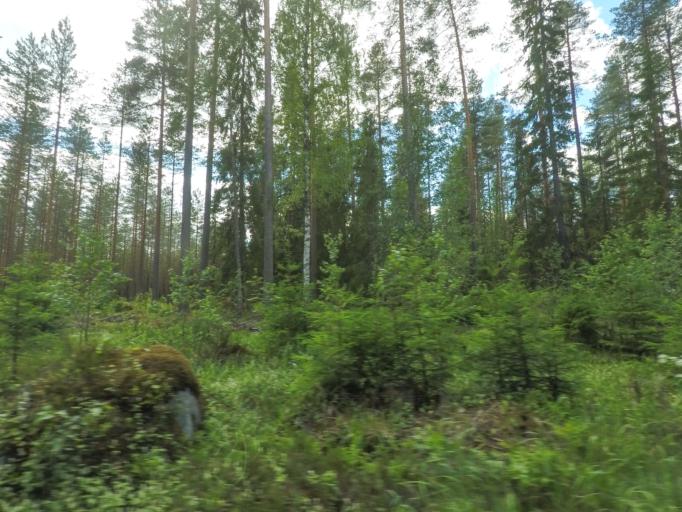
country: FI
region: Central Finland
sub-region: Jyvaeskylae
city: Hankasalmi
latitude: 62.4097
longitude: 26.6485
